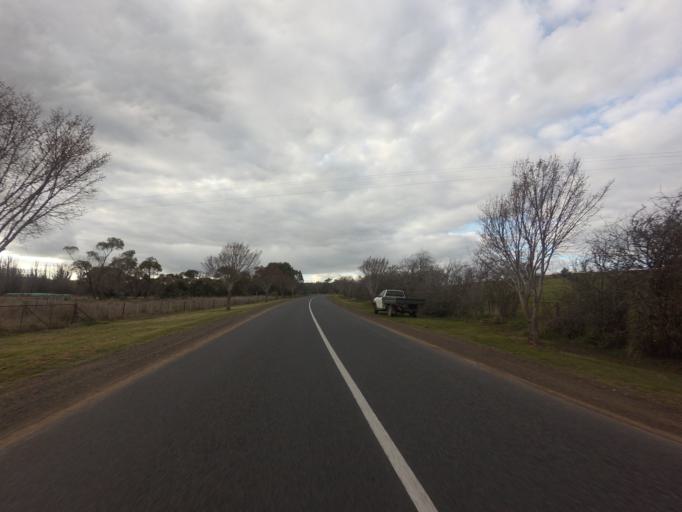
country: AU
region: Tasmania
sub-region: Northern Midlands
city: Evandale
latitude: -42.0166
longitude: 147.4914
